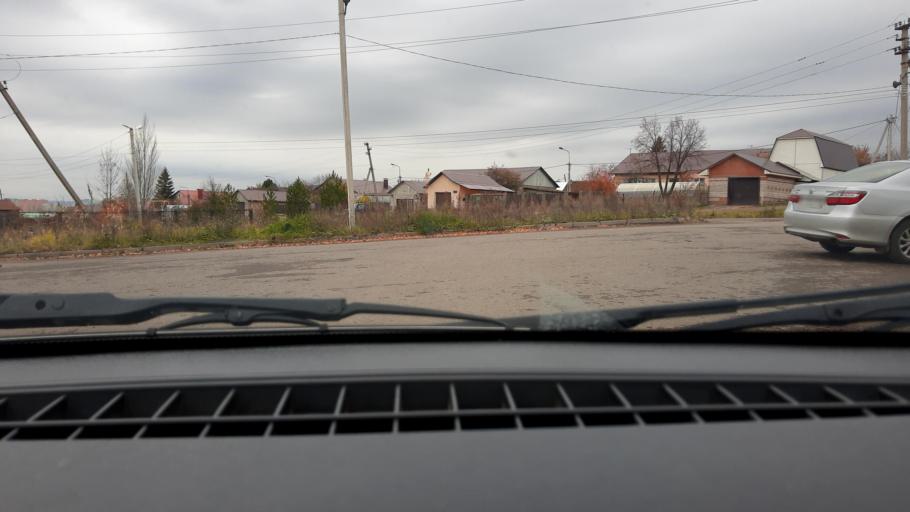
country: RU
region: Bashkortostan
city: Mikhaylovka
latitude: 54.8130
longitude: 55.8943
